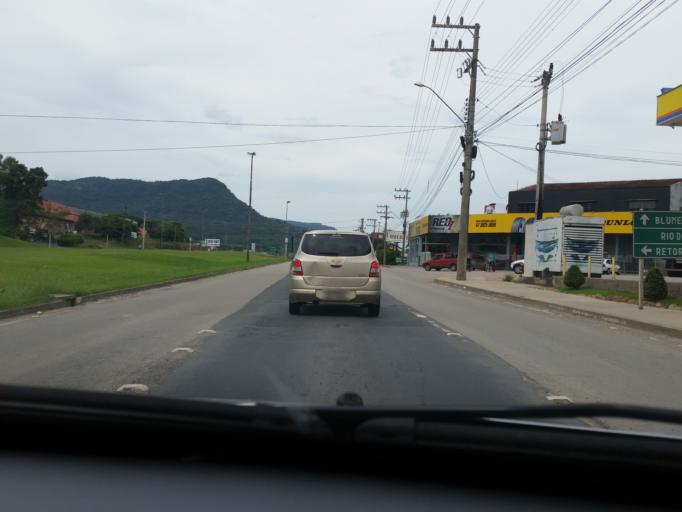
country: BR
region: Santa Catarina
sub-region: Rio Do Sul
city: Rio do Sul
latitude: -27.2022
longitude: -49.6335
